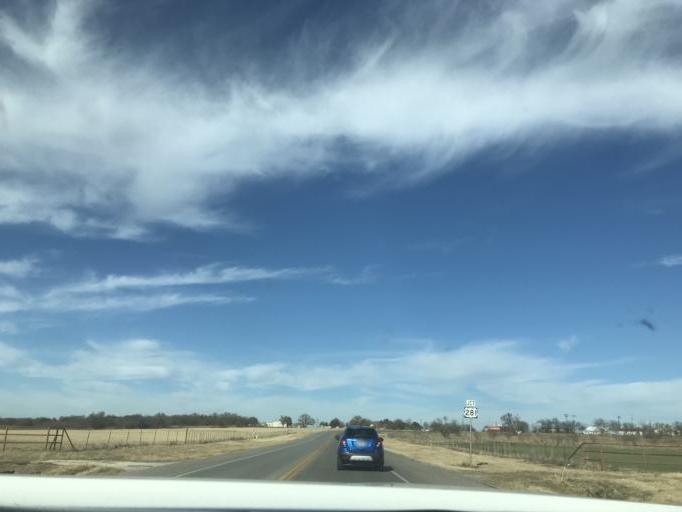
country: US
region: Texas
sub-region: Erath County
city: Stephenville
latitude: 32.2398
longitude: -98.1982
